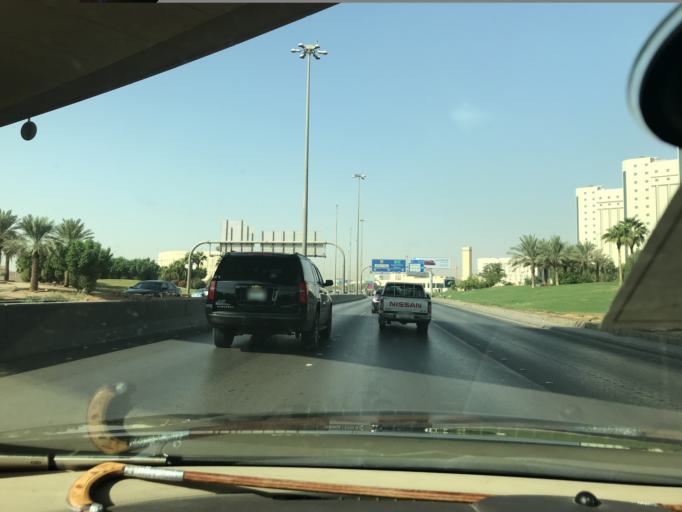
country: SA
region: Ar Riyad
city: Riyadh
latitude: 24.6881
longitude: 46.7114
